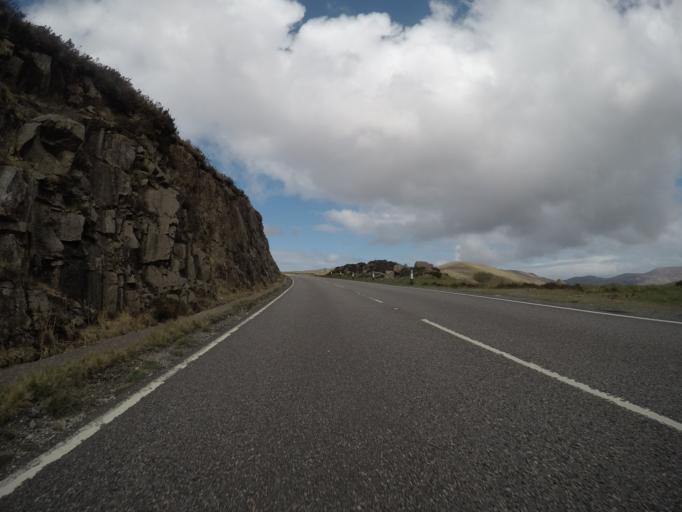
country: GB
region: Scotland
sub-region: Highland
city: Portree
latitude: 57.2689
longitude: -6.0890
